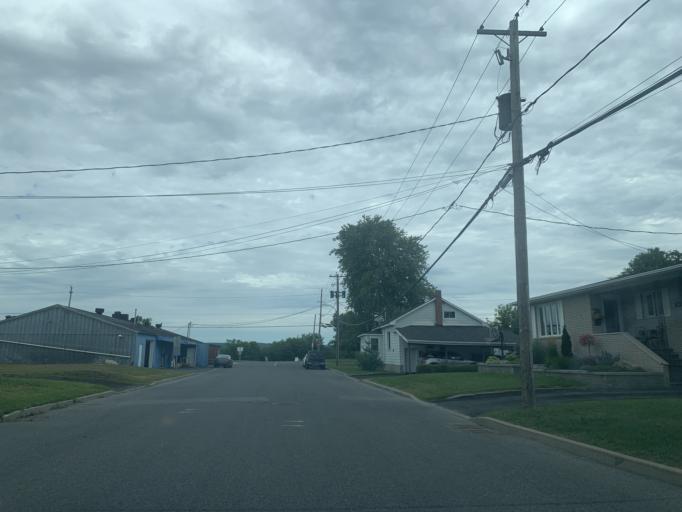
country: CA
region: Ontario
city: Hawkesbury
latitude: 45.6066
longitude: -74.5857
